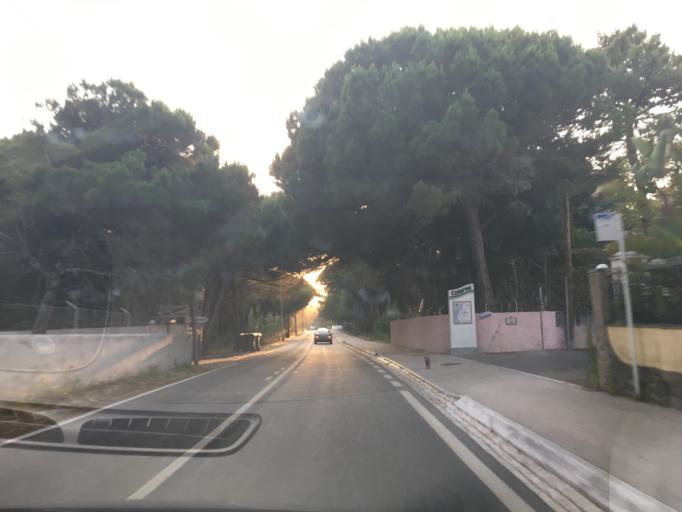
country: PT
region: Lisbon
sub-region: Sintra
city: Colares
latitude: 38.8318
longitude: -9.4495
